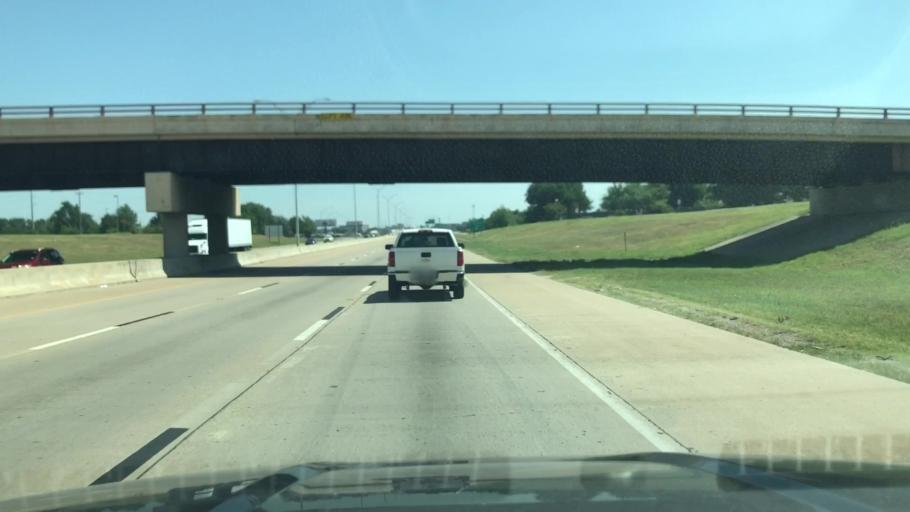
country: US
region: Oklahoma
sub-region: Tulsa County
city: Broken Arrow
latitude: 36.1271
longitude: -95.8760
